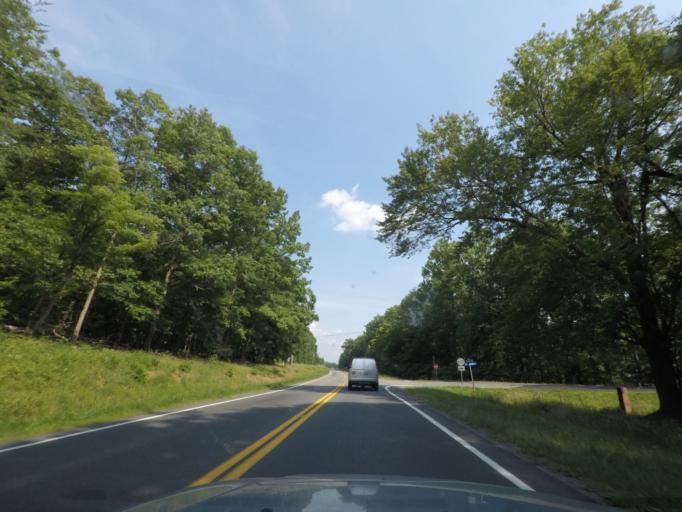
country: US
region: Virginia
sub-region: Fluvanna County
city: Palmyra
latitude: 37.8210
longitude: -78.2671
